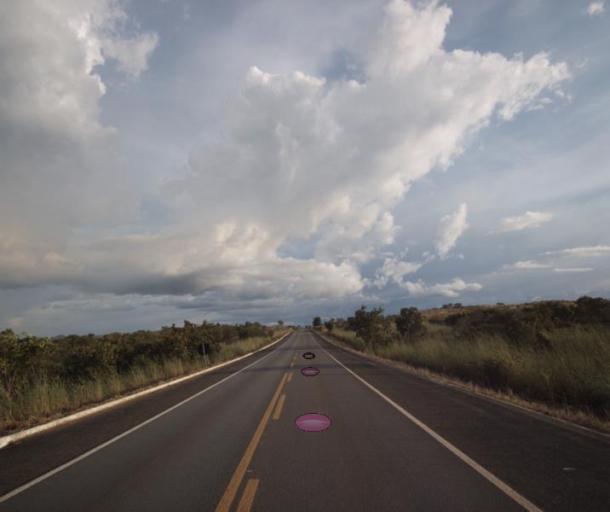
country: BR
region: Goias
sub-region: Barro Alto
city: Barro Alto
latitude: -14.8091
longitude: -48.6355
